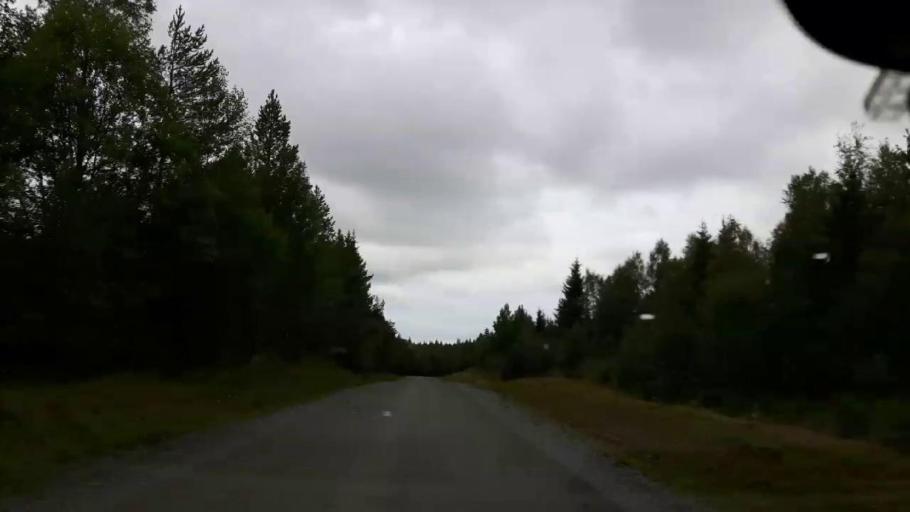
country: SE
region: Jaemtland
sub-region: OEstersunds Kommun
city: Ostersund
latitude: 63.0630
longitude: 14.5528
